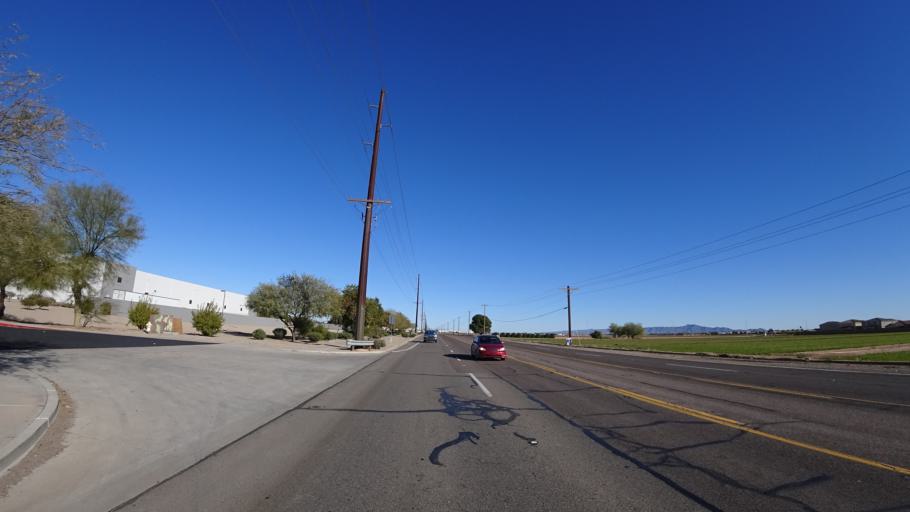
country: US
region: Arizona
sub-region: Maricopa County
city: Tolleson
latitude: 33.4356
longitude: -112.2834
